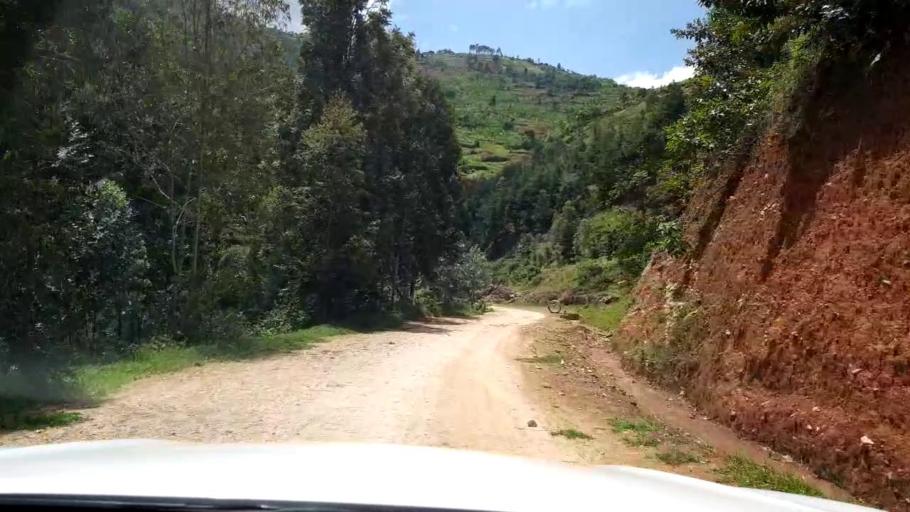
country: RW
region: Southern Province
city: Gitarama
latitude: -1.9852
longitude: 29.6221
